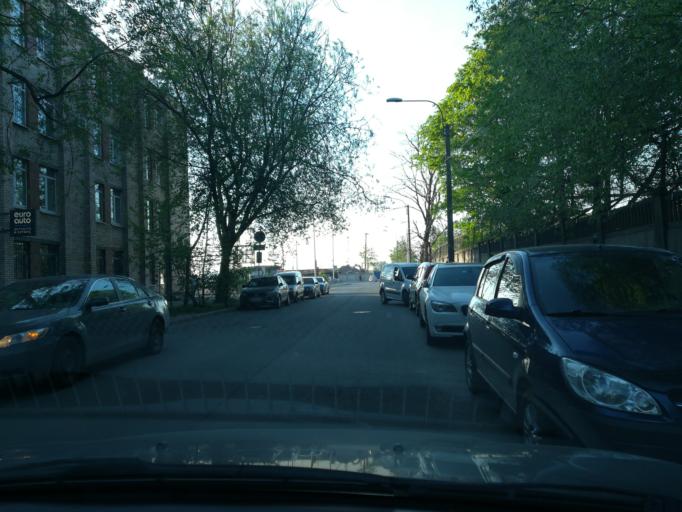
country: RU
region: St.-Petersburg
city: Vasyl'evsky Ostrov
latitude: 59.9547
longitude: 30.2479
